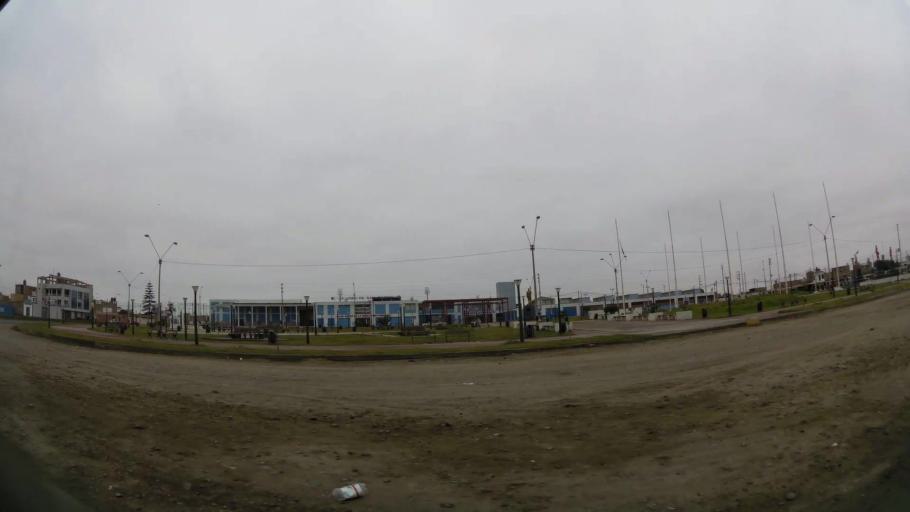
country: PE
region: Ica
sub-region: Provincia de Pisco
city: Pisco
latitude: -13.7167
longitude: -76.2195
